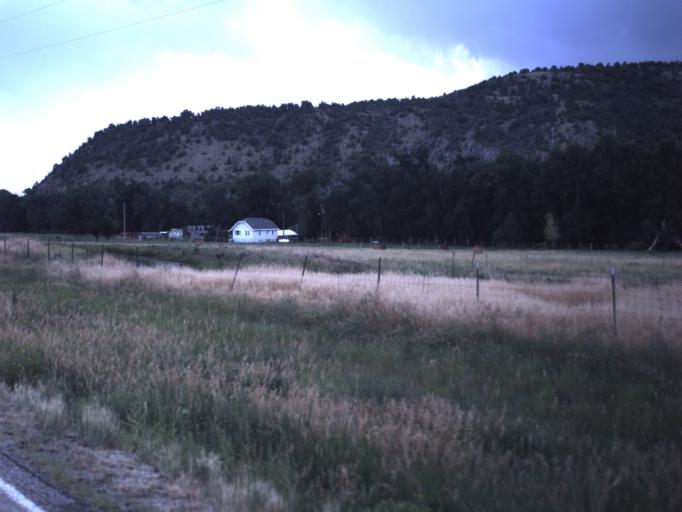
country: US
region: Utah
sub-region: Duchesne County
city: Duchesne
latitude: 40.3983
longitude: -110.7573
